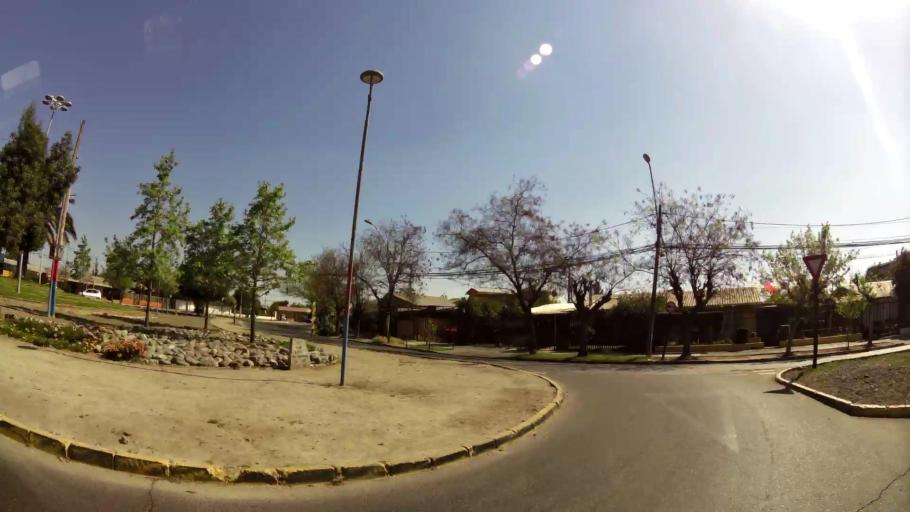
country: CL
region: Santiago Metropolitan
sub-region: Provincia de Santiago
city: La Pintana
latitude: -33.5258
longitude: -70.6071
